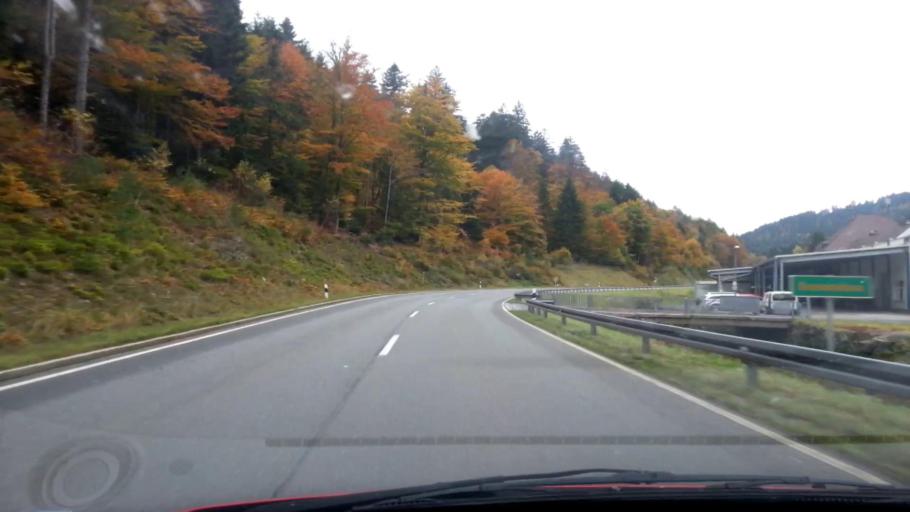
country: DE
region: Bavaria
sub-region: Upper Franconia
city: Warmensteinach
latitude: 49.9660
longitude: 11.7647
